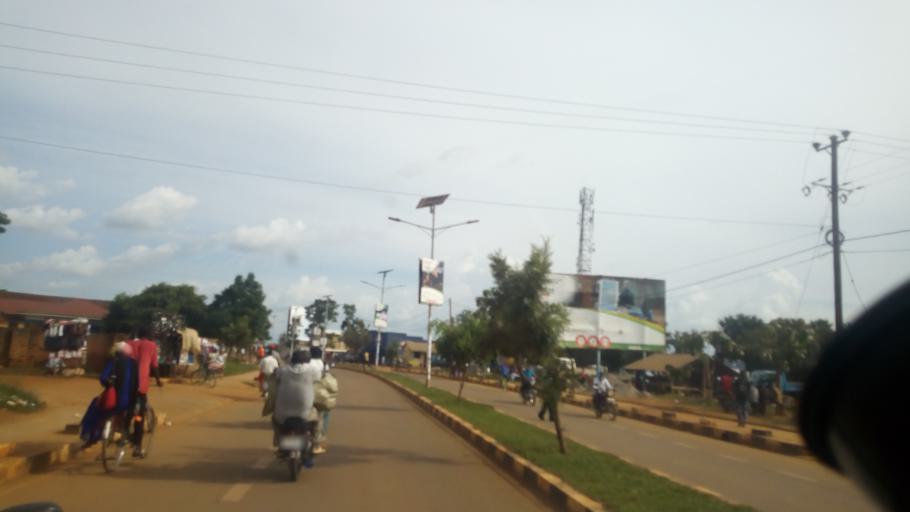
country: UG
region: Northern Region
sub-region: Lira District
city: Lira
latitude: 2.2360
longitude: 32.8932
